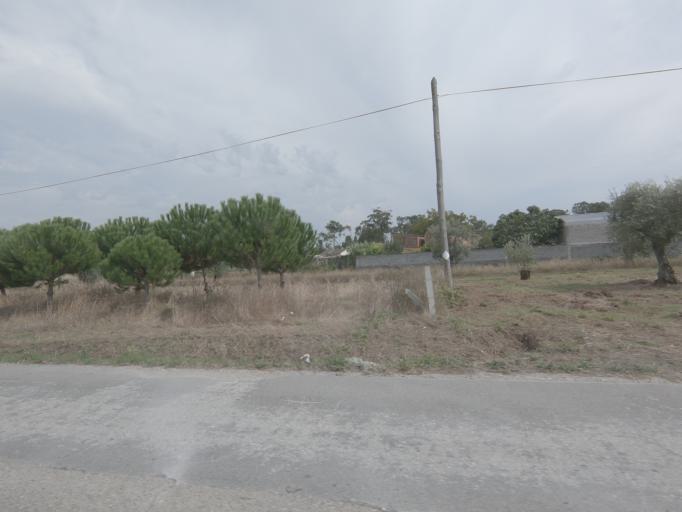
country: PT
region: Leiria
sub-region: Pombal
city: Pombal
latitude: 39.8831
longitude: -8.6745
